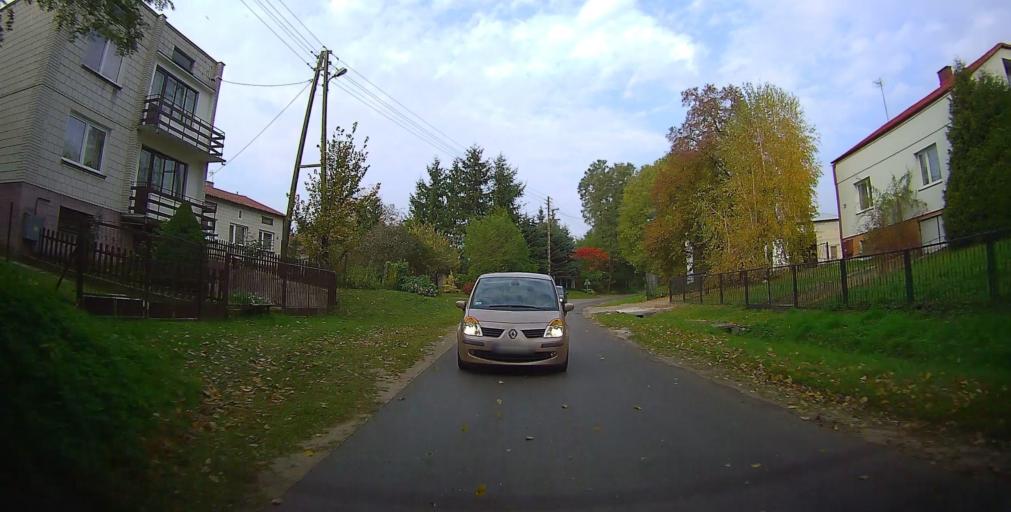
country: PL
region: Masovian Voivodeship
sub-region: Powiat grojecki
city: Mogielnica
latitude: 51.6435
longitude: 20.7394
